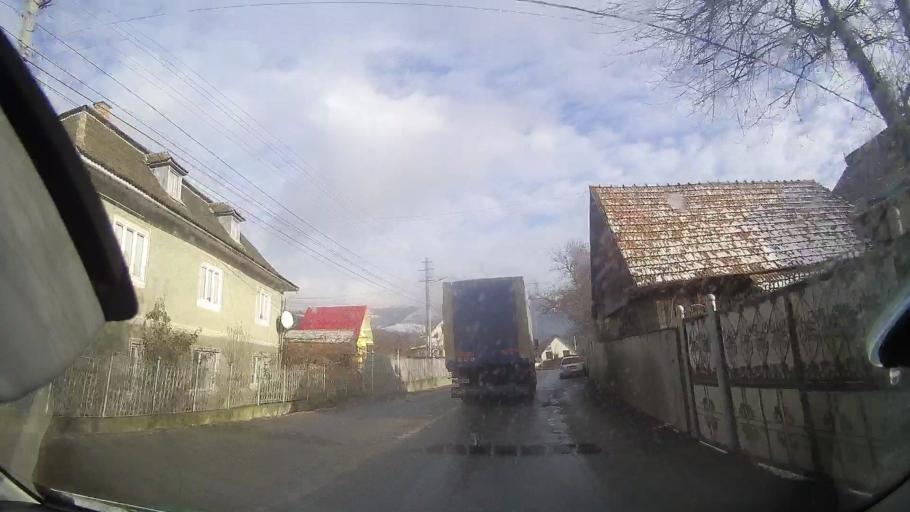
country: RO
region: Alba
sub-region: Comuna Lupsa
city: Lupsa
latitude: 46.3693
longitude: 23.2076
